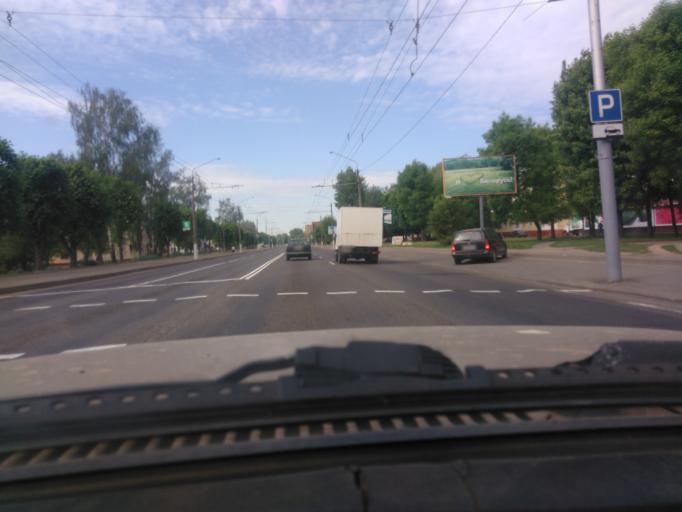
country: BY
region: Mogilev
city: Buynichy
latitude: 53.8842
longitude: 30.2726
